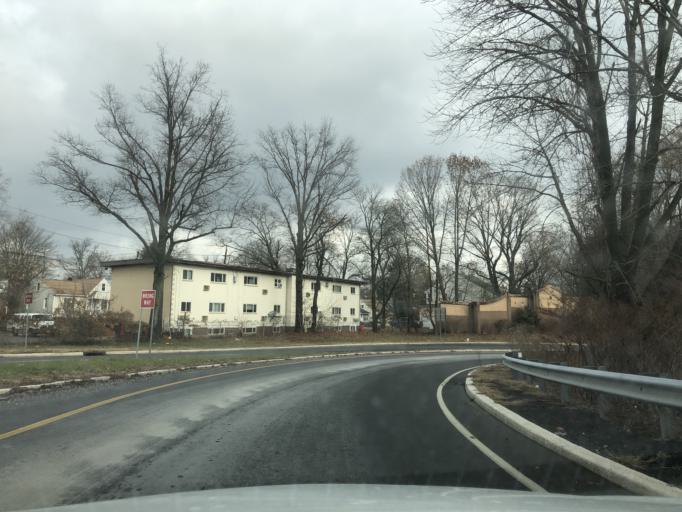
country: US
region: New Jersey
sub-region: Camden County
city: Mount Ephraim
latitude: 39.8731
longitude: -75.0822
